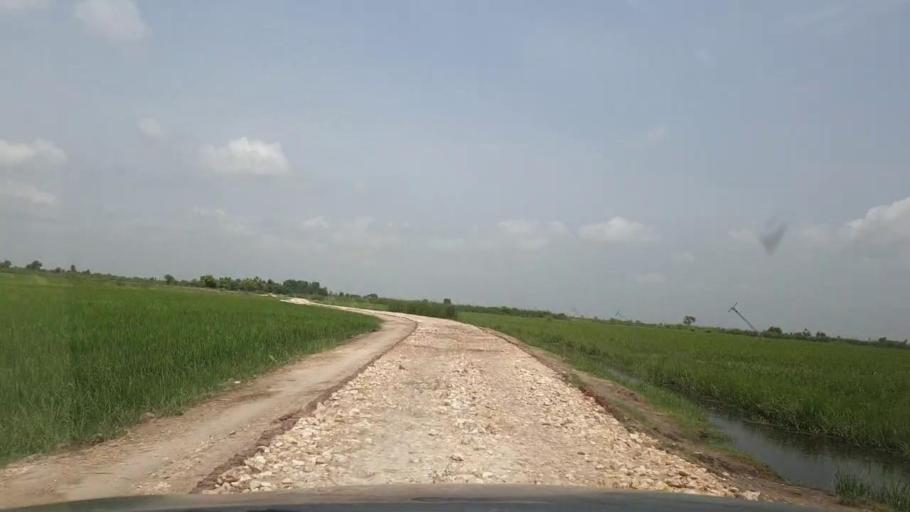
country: PK
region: Sindh
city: Ratodero
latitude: 27.9184
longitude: 68.3070
